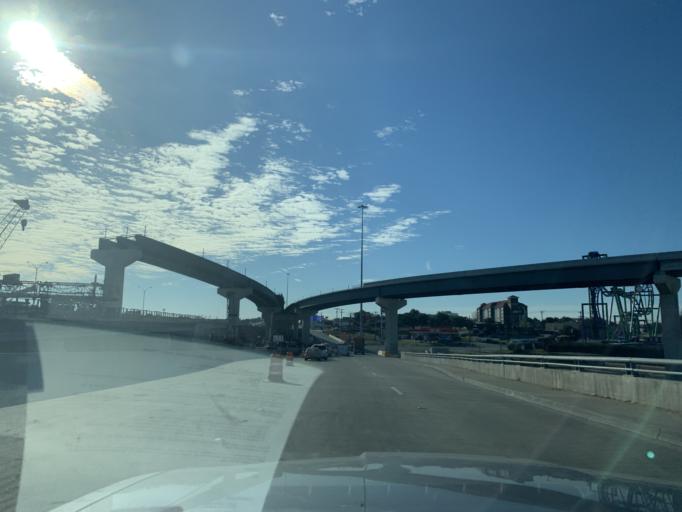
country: US
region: Texas
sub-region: Tarrant County
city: Arlington
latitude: 32.7590
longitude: -97.0643
